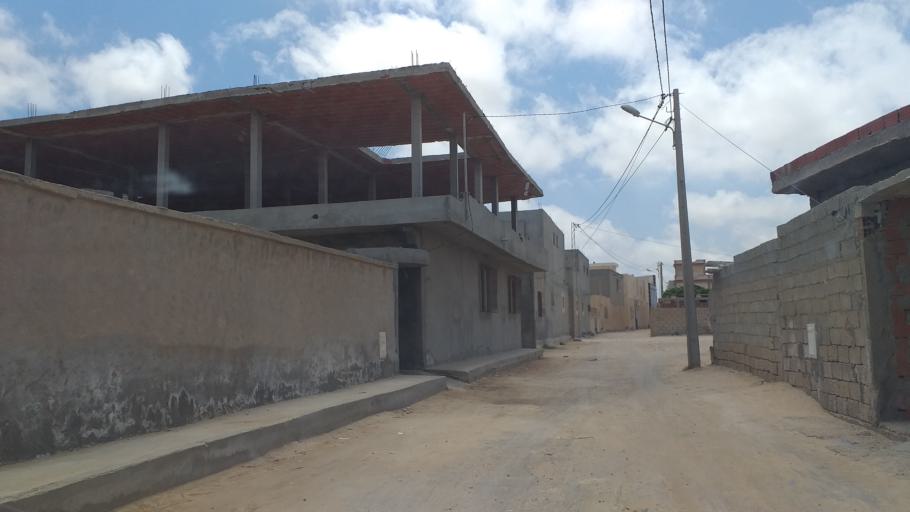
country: TN
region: Qabis
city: Gabes
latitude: 33.9353
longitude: 10.0621
